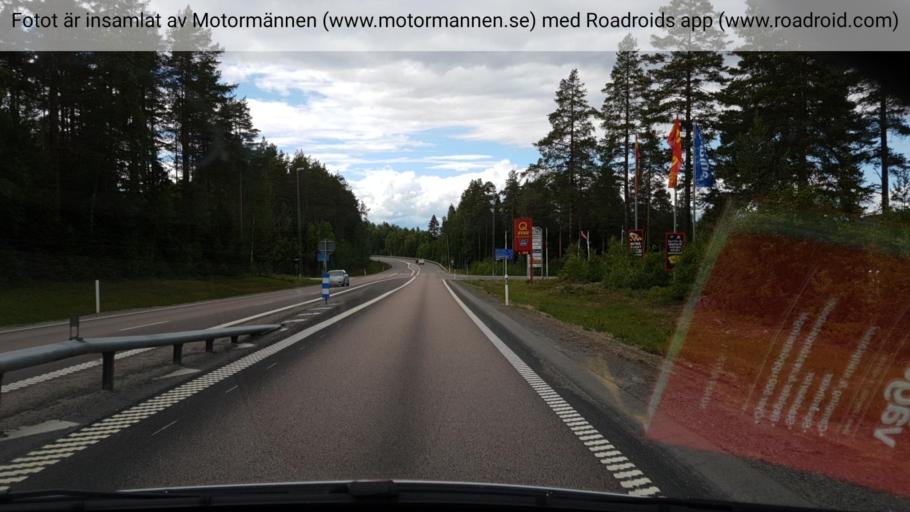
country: SE
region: Vaesternorrland
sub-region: Solleftea Kommun
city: Solleftea
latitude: 63.1735
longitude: 17.0595
